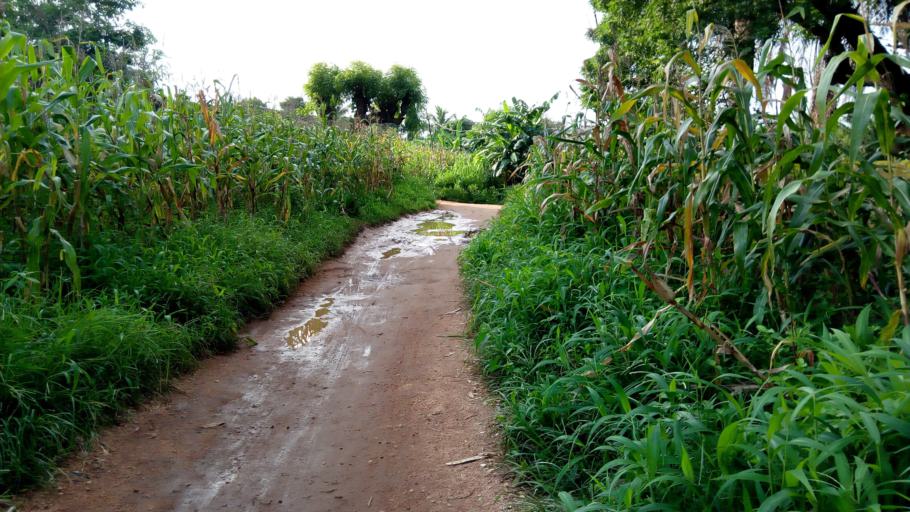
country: TG
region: Kara
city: Kara
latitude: 9.5599
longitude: 1.2100
